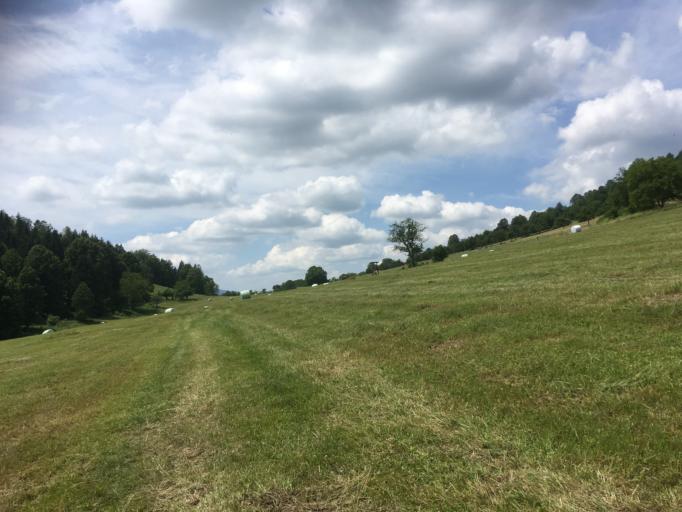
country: SI
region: Kocevje
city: Kocevje
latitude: 45.6109
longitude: 14.9655
